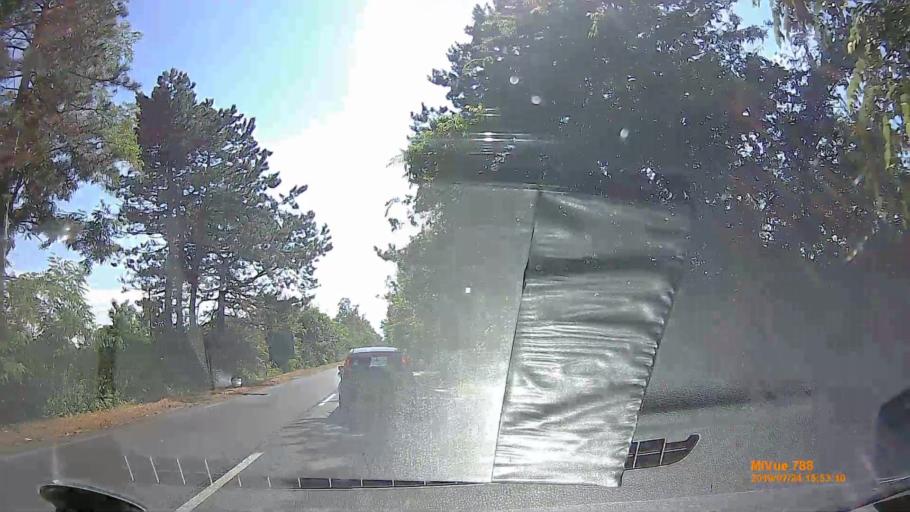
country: HU
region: Szabolcs-Szatmar-Bereg
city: Vaja
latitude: 48.0225
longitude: 22.1533
